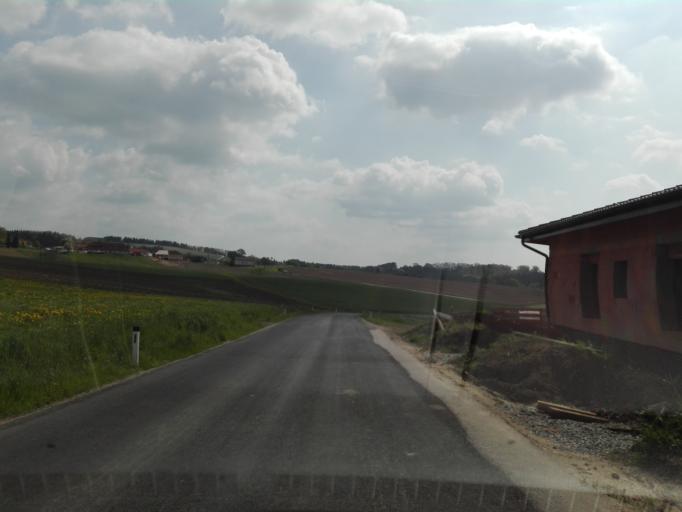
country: AT
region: Upper Austria
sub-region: Politischer Bezirk Perg
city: Perg
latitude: 48.2410
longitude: 14.6990
